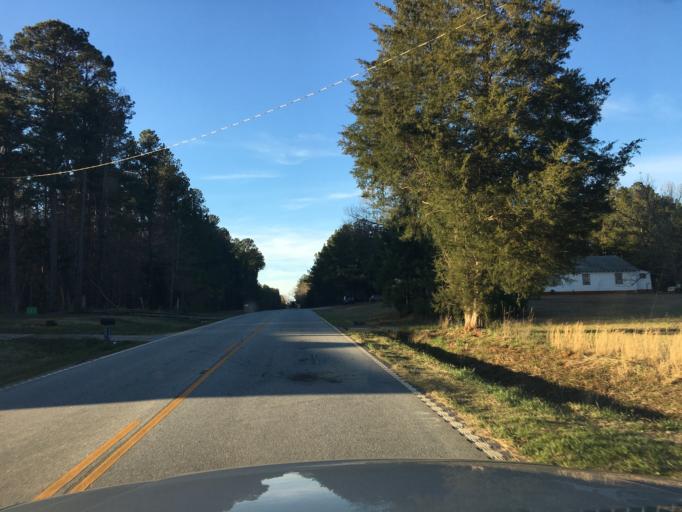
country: US
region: South Carolina
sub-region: Saluda County
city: Saluda
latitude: 34.0772
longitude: -81.8207
